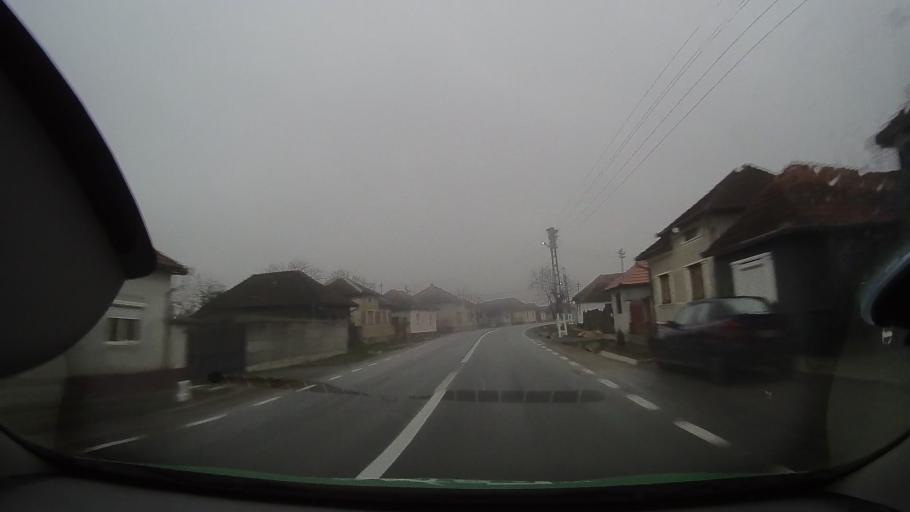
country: RO
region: Arad
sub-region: Comuna Craiova
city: Craiova
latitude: 46.6308
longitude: 21.9587
